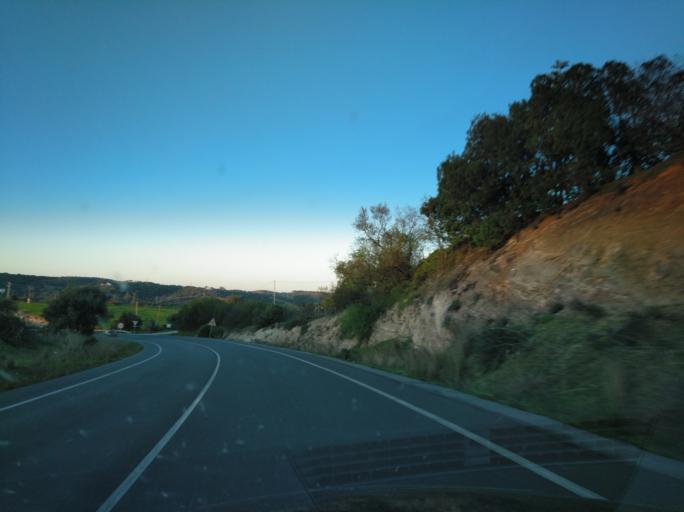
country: ES
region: Andalusia
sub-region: Provincia de Huelva
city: Ayamonte
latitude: 37.2288
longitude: -7.4009
